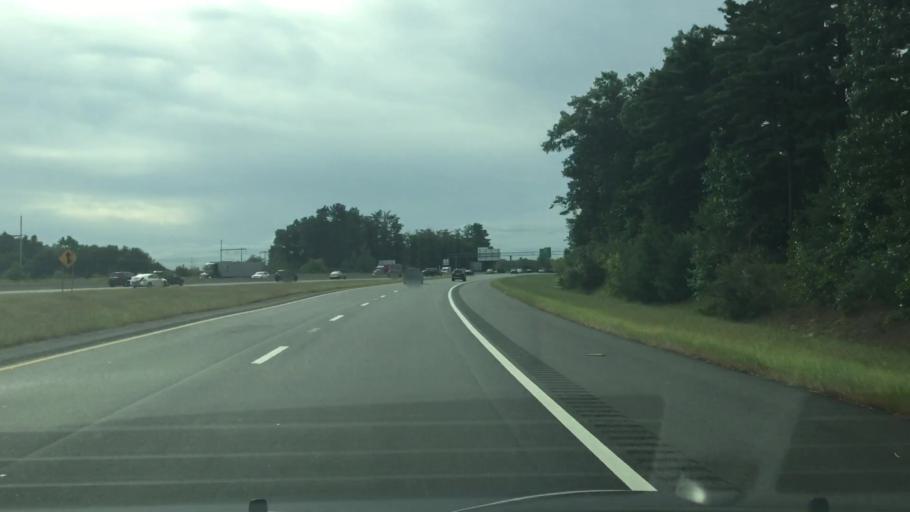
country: US
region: Massachusetts
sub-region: Middlesex County
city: Lowell
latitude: 42.5960
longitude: -71.3195
